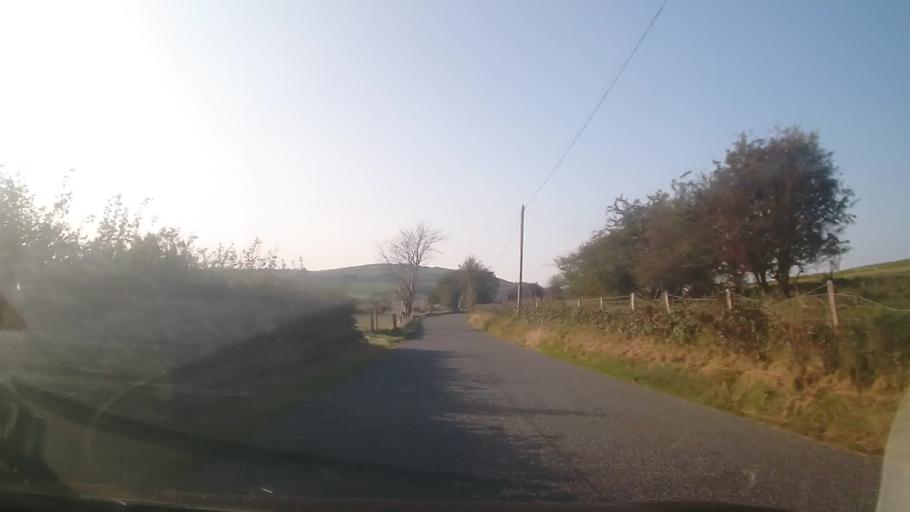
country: GB
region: Wales
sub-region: County of Ceredigion
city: Lledrod
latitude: 52.3588
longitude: -3.8493
